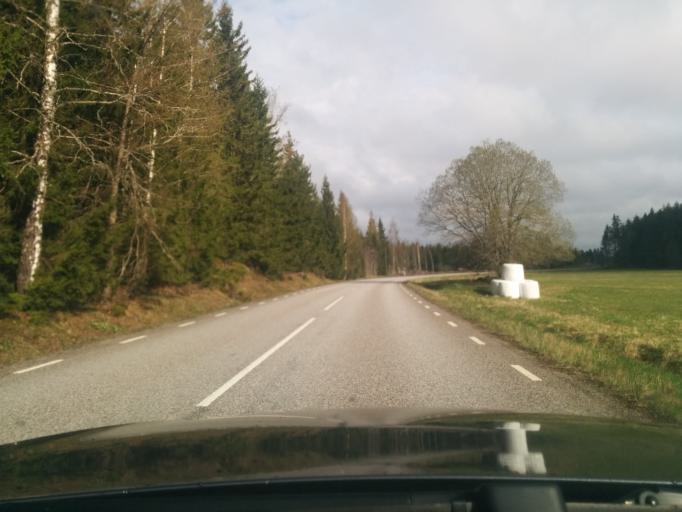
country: SE
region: Uppsala
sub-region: Tierps Kommun
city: Orbyhus
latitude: 60.2046
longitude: 17.6997
